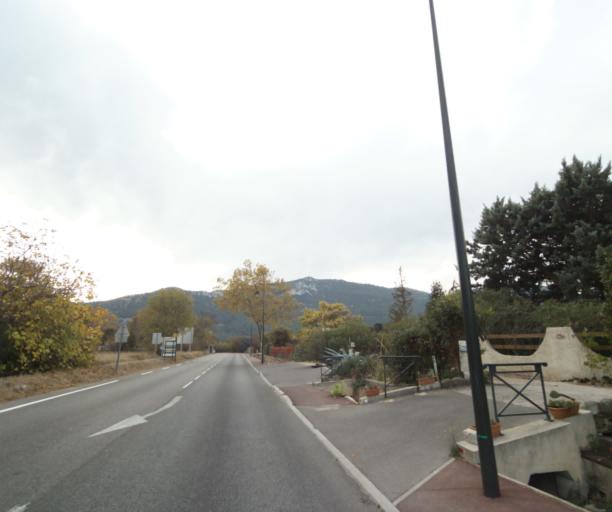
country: FR
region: Provence-Alpes-Cote d'Azur
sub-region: Departement des Bouches-du-Rhone
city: Gemenos
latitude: 43.2886
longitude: 5.6248
